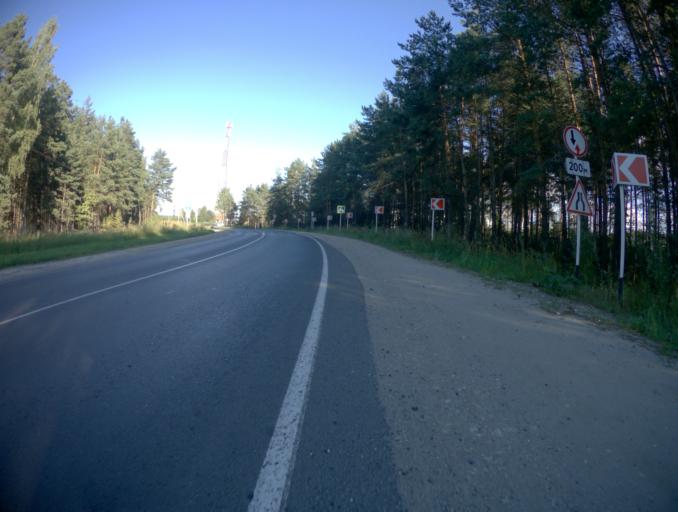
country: RU
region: Vladimir
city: Raduzhnyy
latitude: 56.0229
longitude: 40.3825
